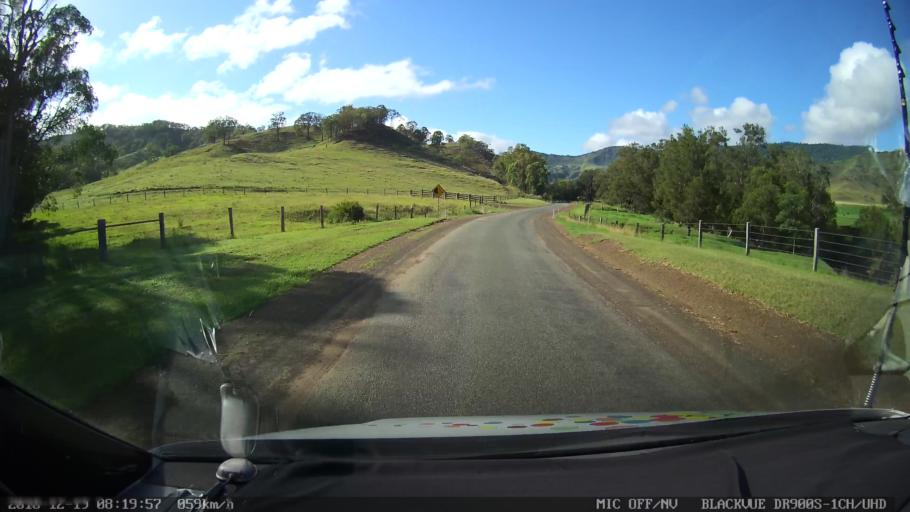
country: AU
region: New South Wales
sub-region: Kyogle
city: Kyogle
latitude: -28.2865
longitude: 152.9099
